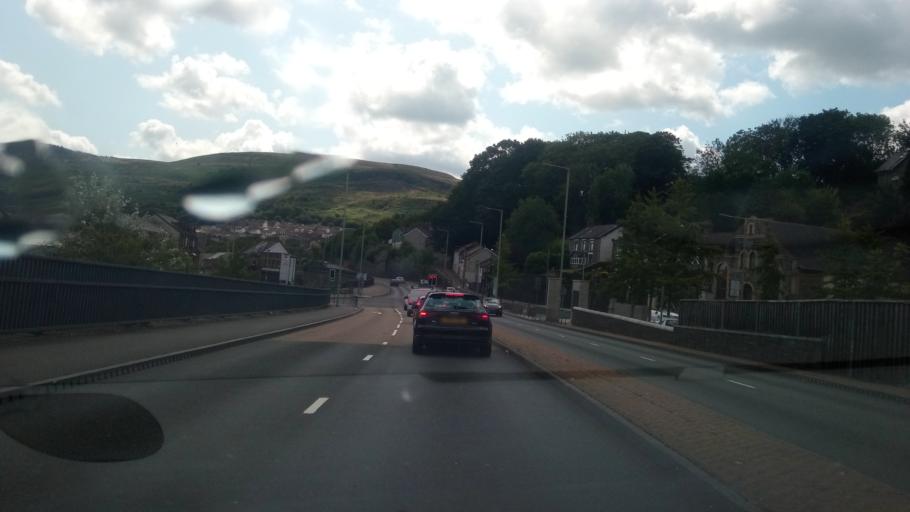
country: GB
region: Wales
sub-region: Rhondda Cynon Taf
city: Porth
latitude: 51.6129
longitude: -3.4103
